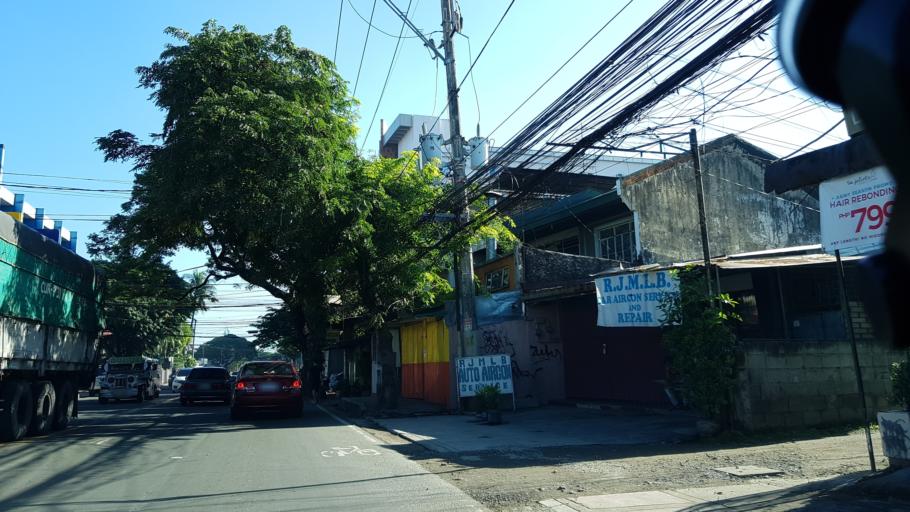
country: PH
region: Metro Manila
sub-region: Pasig
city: Pasig City
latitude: 14.5753
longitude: 121.0846
